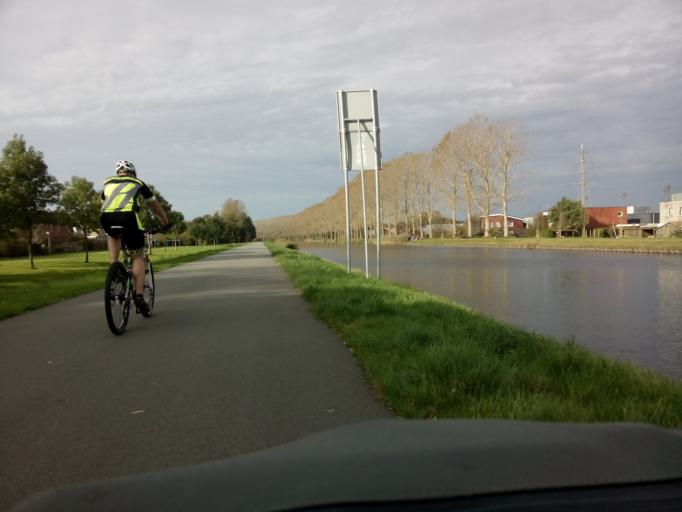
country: NL
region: Drenthe
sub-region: Gemeente Assen
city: Assen
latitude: 53.0219
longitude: 6.5655
